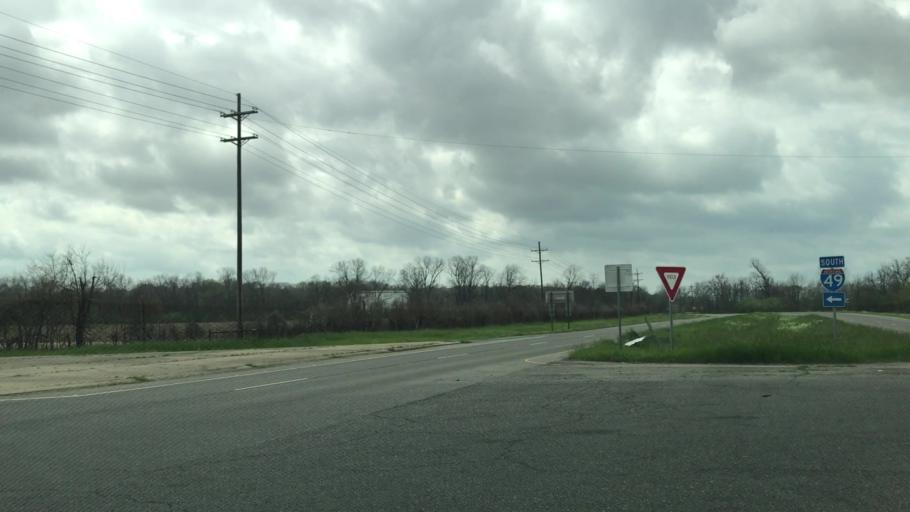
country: US
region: Louisiana
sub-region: Rapides Parish
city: Boyce
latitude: 31.3787
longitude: -92.6697
